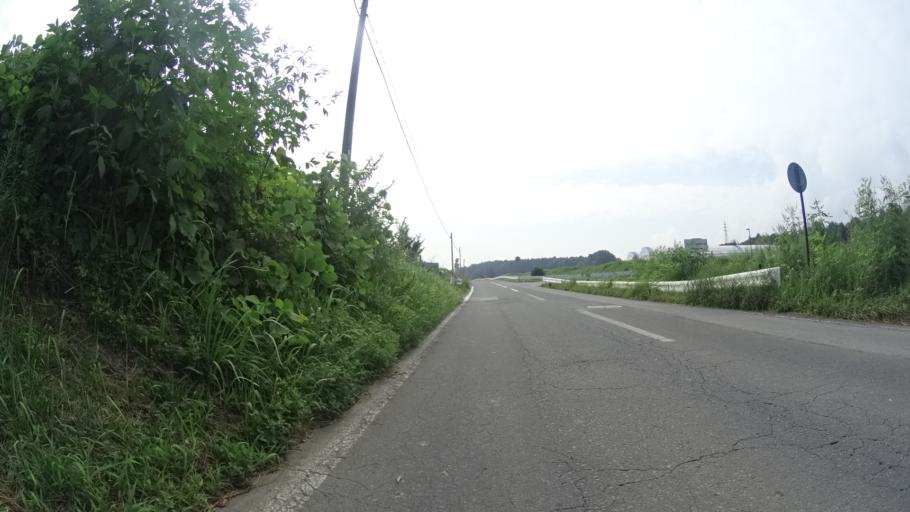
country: JP
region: Nagano
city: Chino
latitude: 35.9719
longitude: 138.1834
